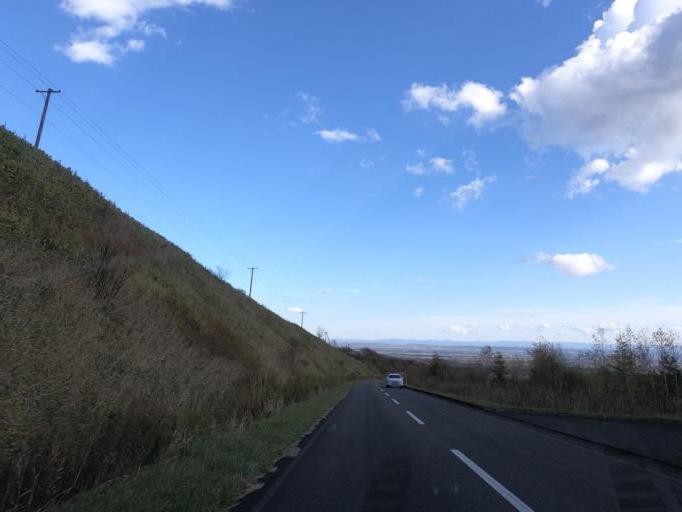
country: JP
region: Hokkaido
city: Otofuke
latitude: 43.2931
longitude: 143.1940
